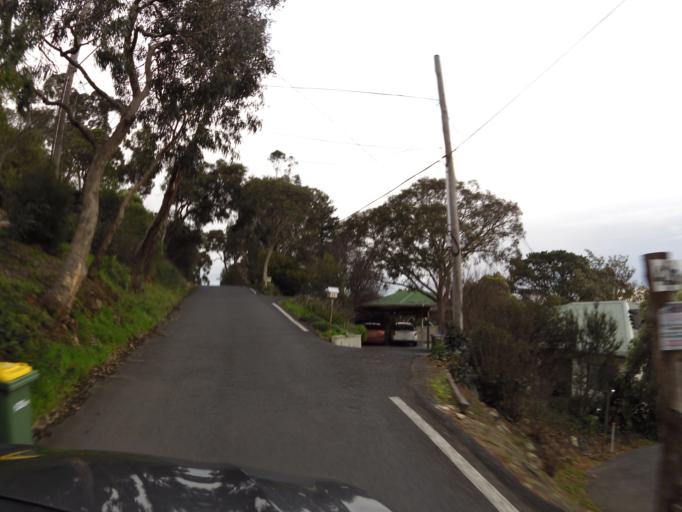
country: AU
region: Victoria
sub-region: Knox
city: Ferntree Gully
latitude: -37.8972
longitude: 145.3040
